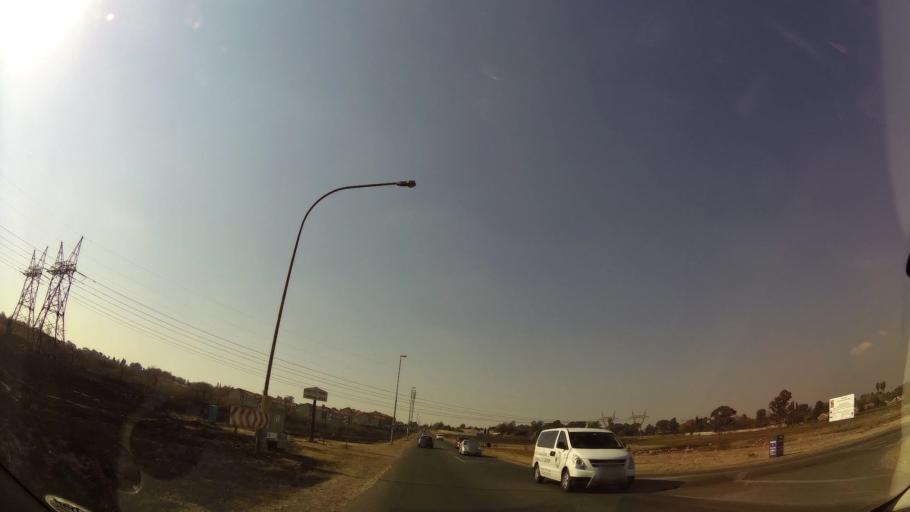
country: ZA
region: Gauteng
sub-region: Ekurhuleni Metropolitan Municipality
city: Benoni
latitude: -26.1412
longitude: 28.2856
